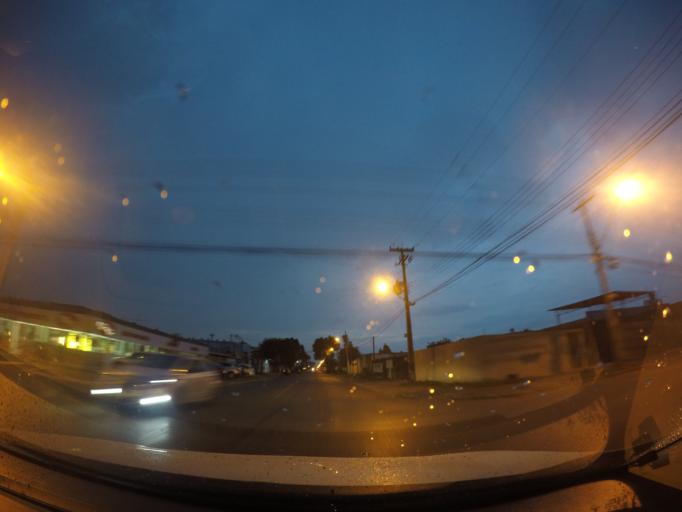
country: BR
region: Parana
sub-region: Sao Jose Dos Pinhais
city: Sao Jose dos Pinhais
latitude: -25.5054
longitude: -49.2317
